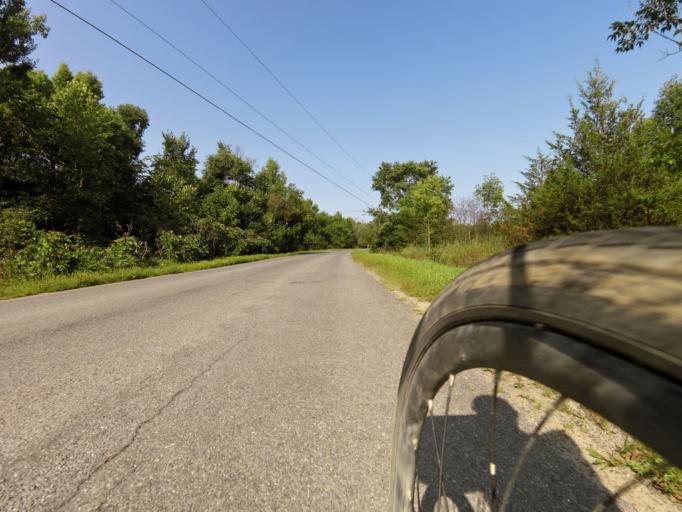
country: CA
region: Ontario
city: Kingston
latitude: 44.3318
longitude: -76.6688
